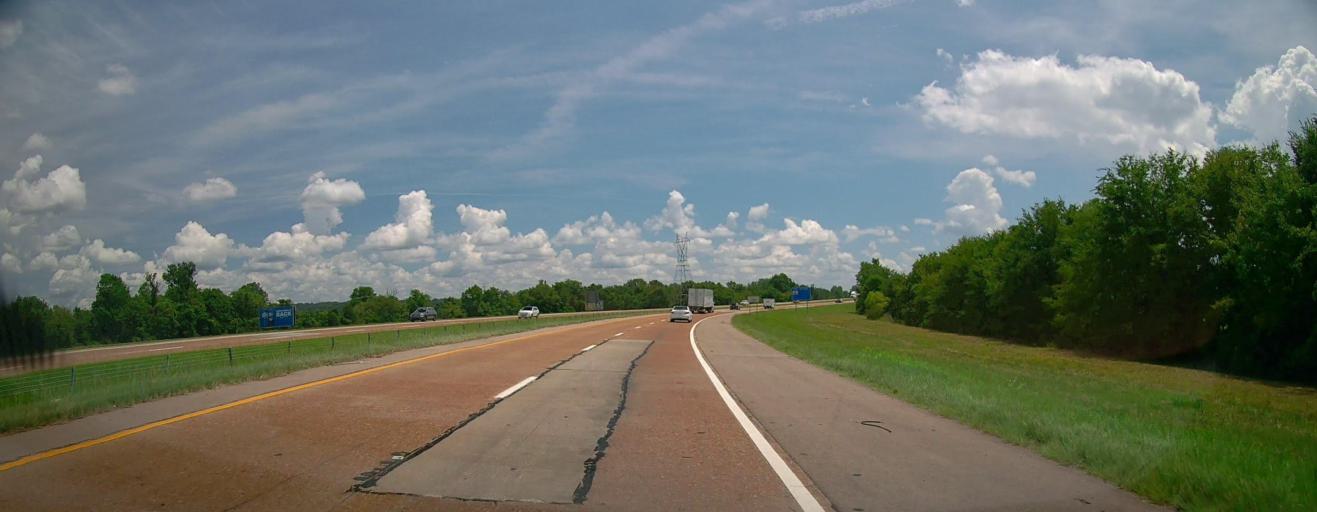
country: US
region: Mississippi
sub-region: Lee County
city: Tupelo
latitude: 34.2673
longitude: -88.6953
